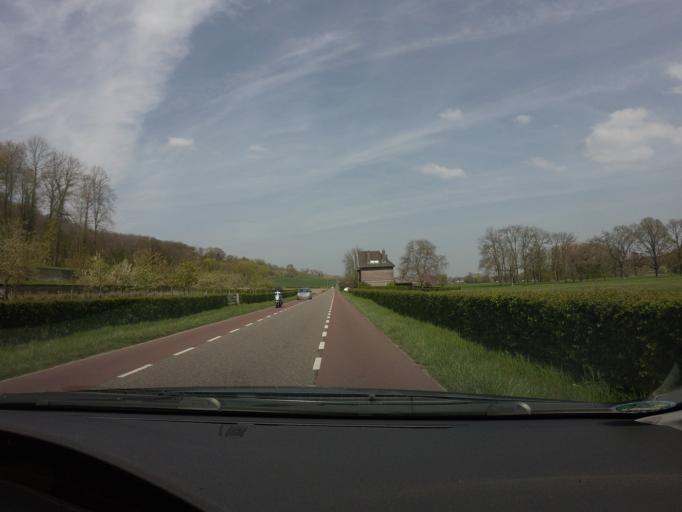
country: NL
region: Limburg
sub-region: Gemeente Maastricht
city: Maastricht
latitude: 50.8197
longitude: 5.6680
